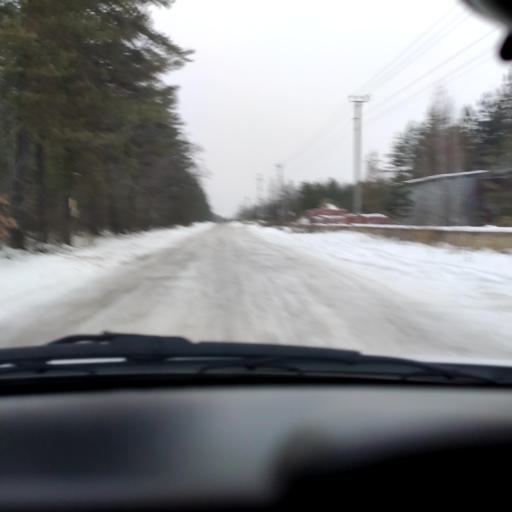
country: RU
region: Voronezj
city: Ramon'
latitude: 51.8875
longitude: 39.2522
